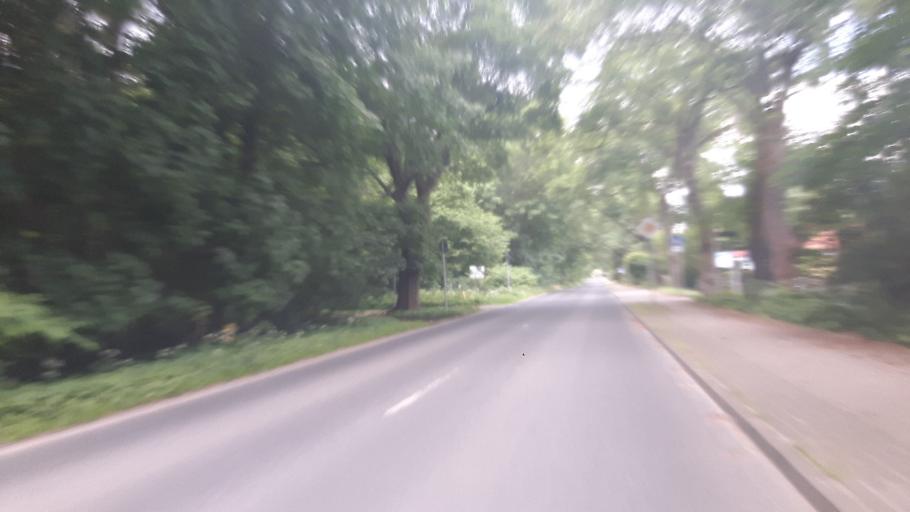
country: DE
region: Brandenburg
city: Bernau bei Berlin
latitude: 52.6496
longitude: 13.5879
